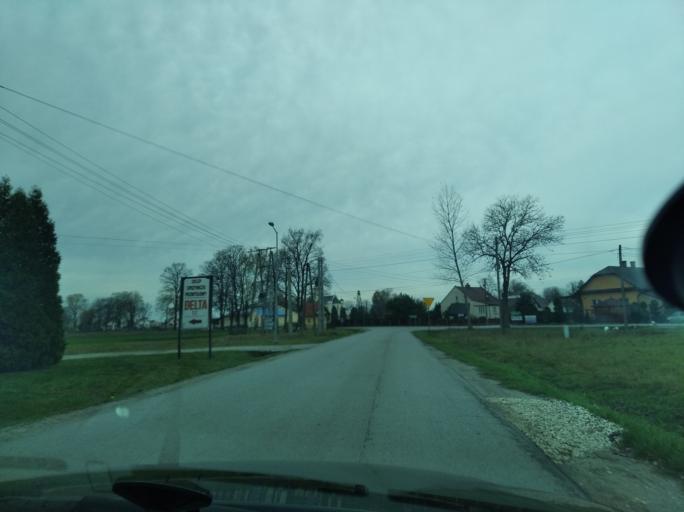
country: PL
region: Subcarpathian Voivodeship
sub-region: Powiat przeworski
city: Grzeska
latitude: 50.0946
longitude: 22.4383
